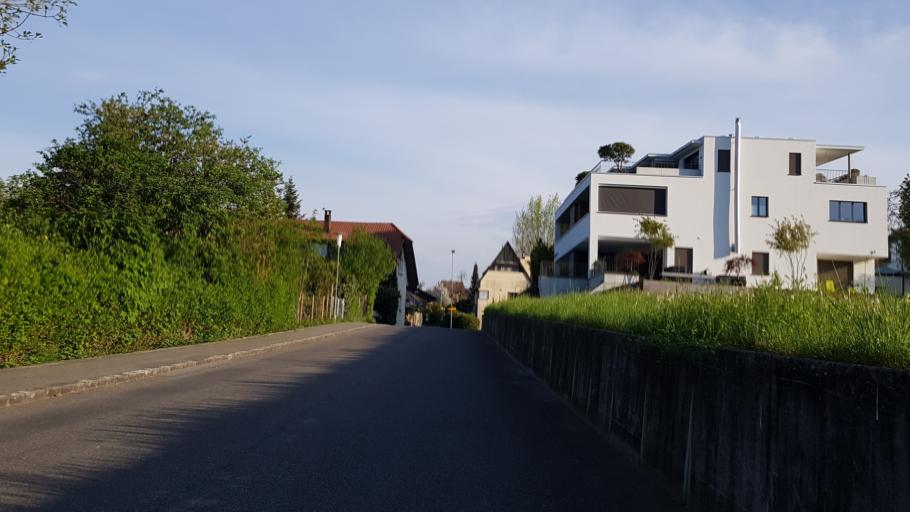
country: CH
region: Aargau
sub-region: Bezirk Kulm
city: Reinach
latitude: 47.2693
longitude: 8.2091
